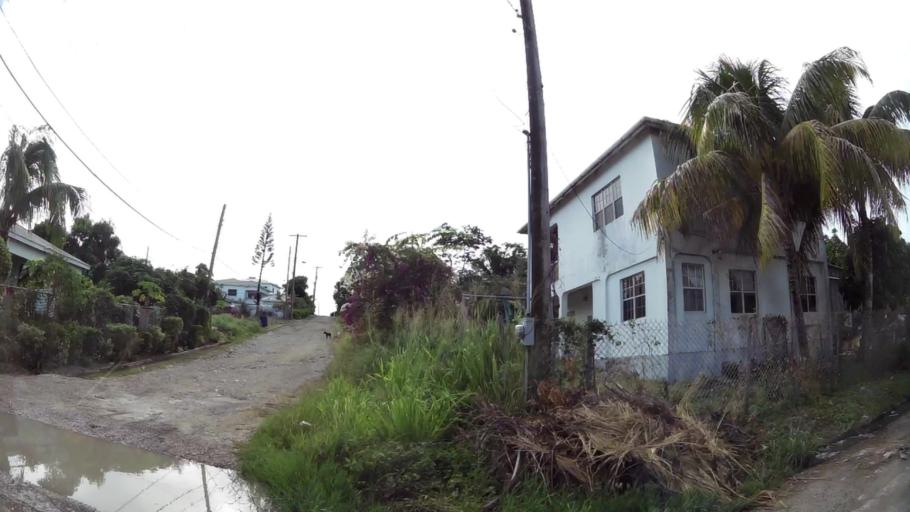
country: AG
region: Saint George
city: Piggotts
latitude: 17.1105
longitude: -61.8145
